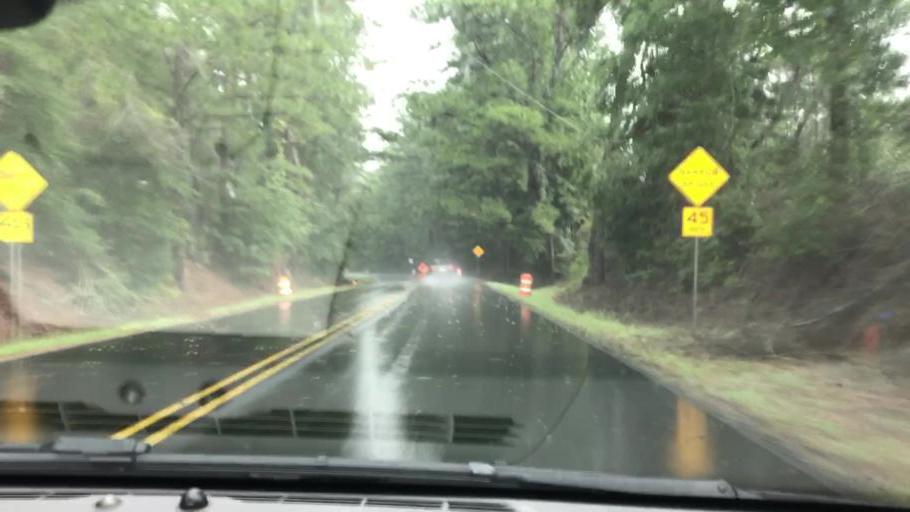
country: US
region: Georgia
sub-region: Clay County
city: Fort Gaines
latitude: 31.5478
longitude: -85.0189
